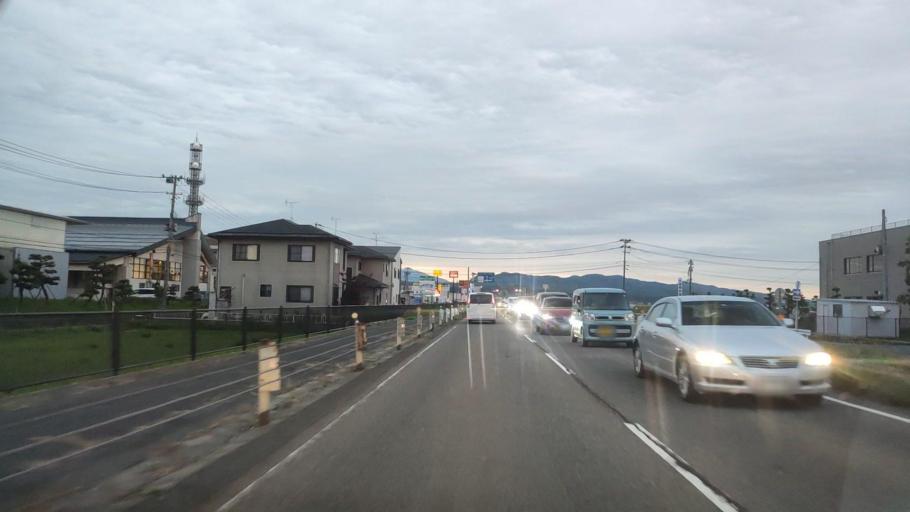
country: JP
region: Niigata
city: Niitsu-honcho
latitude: 37.7888
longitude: 139.1115
